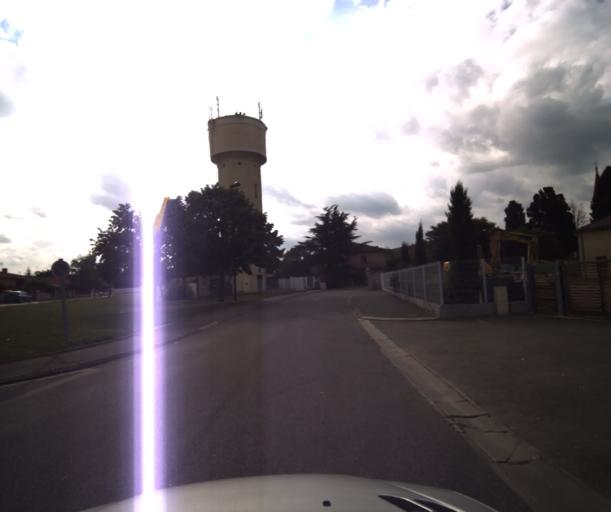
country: FR
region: Midi-Pyrenees
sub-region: Departement de la Haute-Garonne
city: Labarthe-sur-Leze
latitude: 43.4507
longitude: 1.3999
